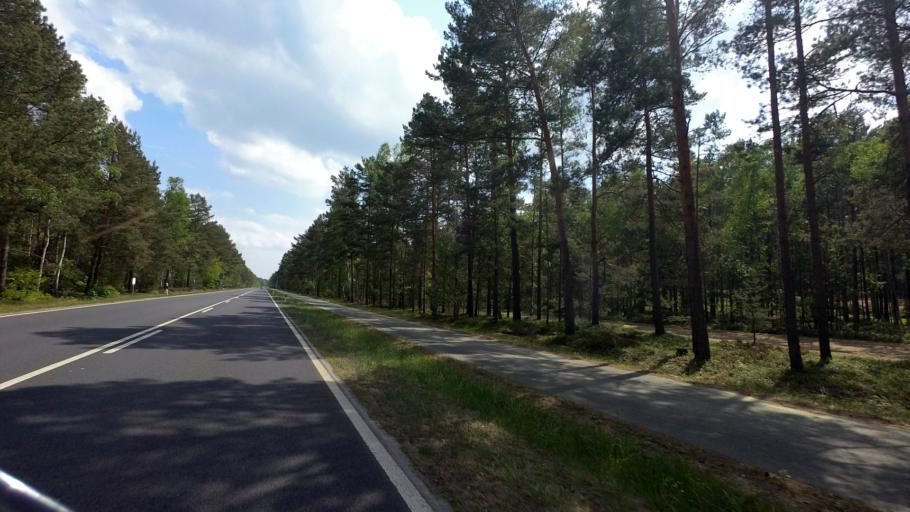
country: DE
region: Saxony
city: Rietschen
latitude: 51.4518
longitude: 14.7645
